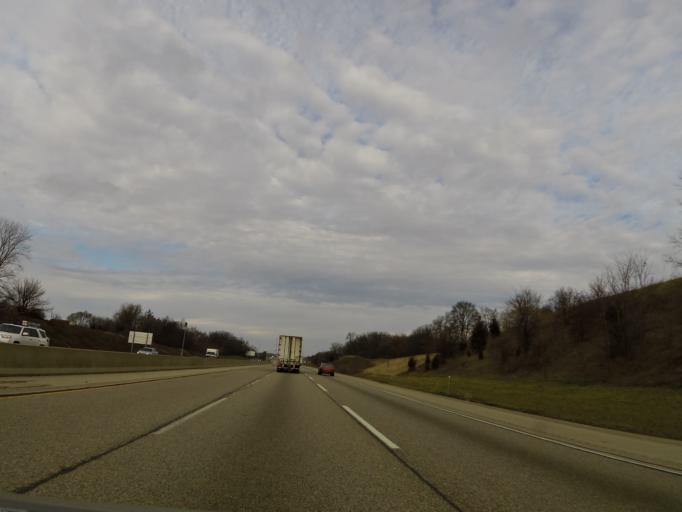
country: US
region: Illinois
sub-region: Winnebago County
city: Roscoe
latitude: 42.4298
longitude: -88.9870
